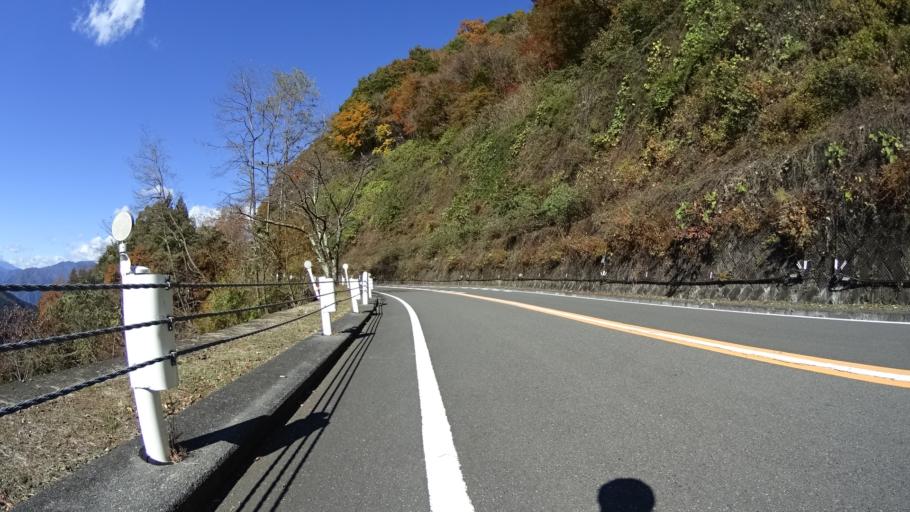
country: JP
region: Yamanashi
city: Uenohara
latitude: 35.7604
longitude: 139.0366
